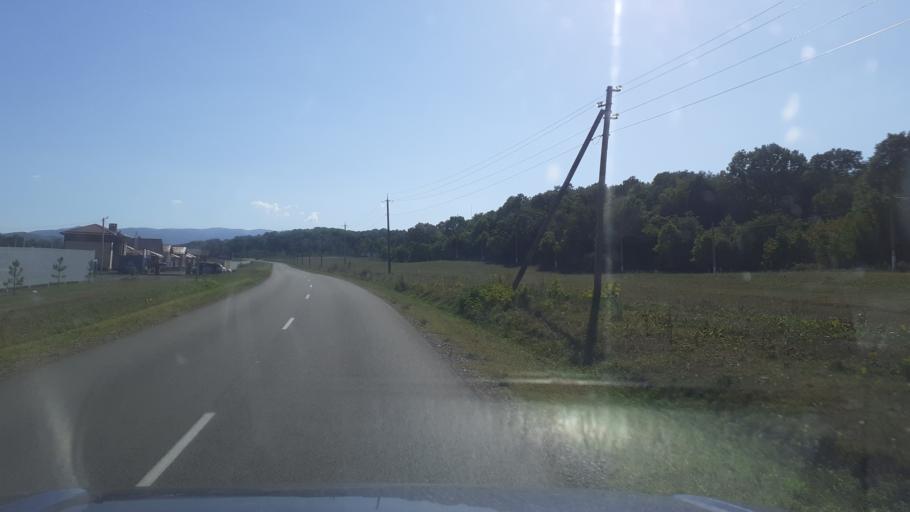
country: RU
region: Krasnodarskiy
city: Azovskaya
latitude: 44.7726
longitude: 38.5756
